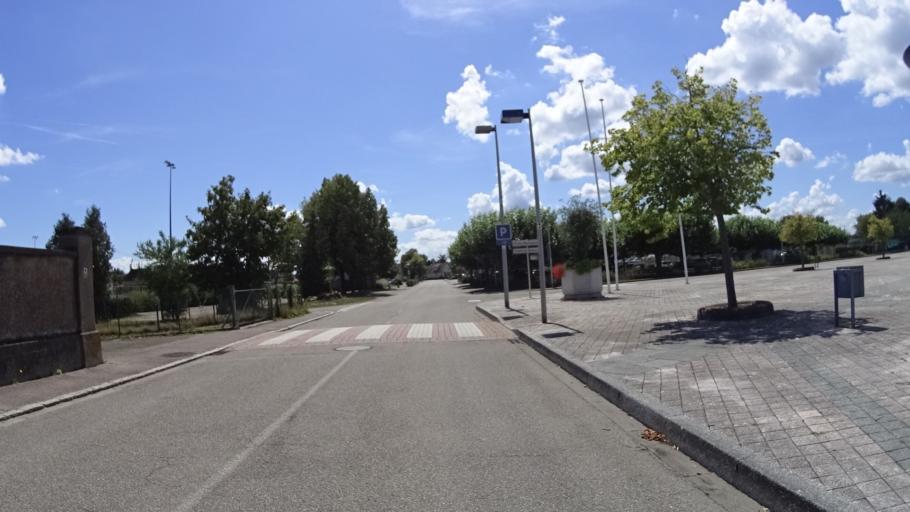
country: FR
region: Alsace
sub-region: Departement du Haut-Rhin
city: Ottmarsheim
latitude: 47.7876
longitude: 7.5032
